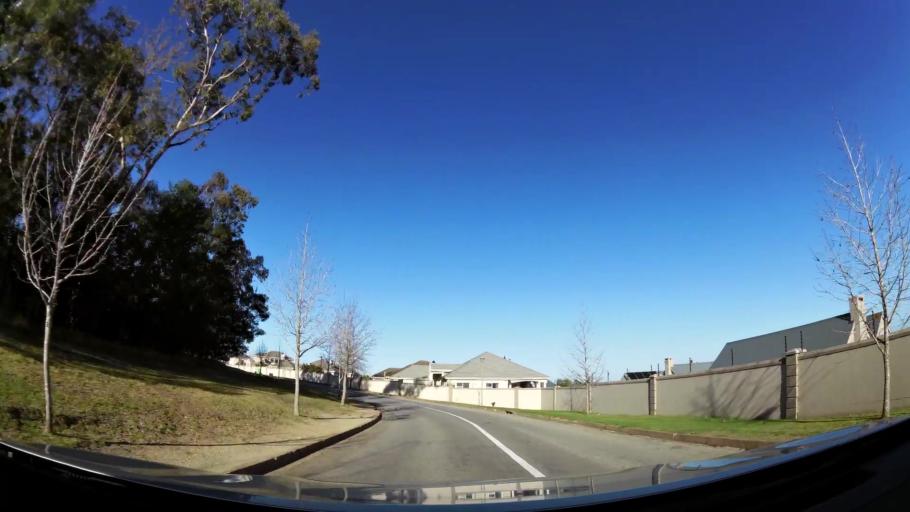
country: ZA
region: Western Cape
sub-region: Eden District Municipality
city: George
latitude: -33.9650
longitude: 22.4384
